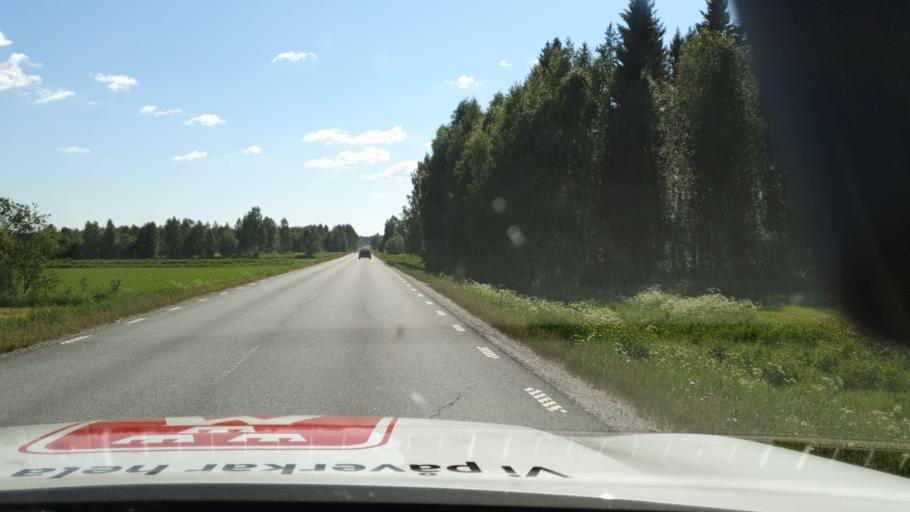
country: SE
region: Vaesterbotten
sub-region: Skelleftea Kommun
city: Viken
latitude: 64.6058
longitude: 20.9498
